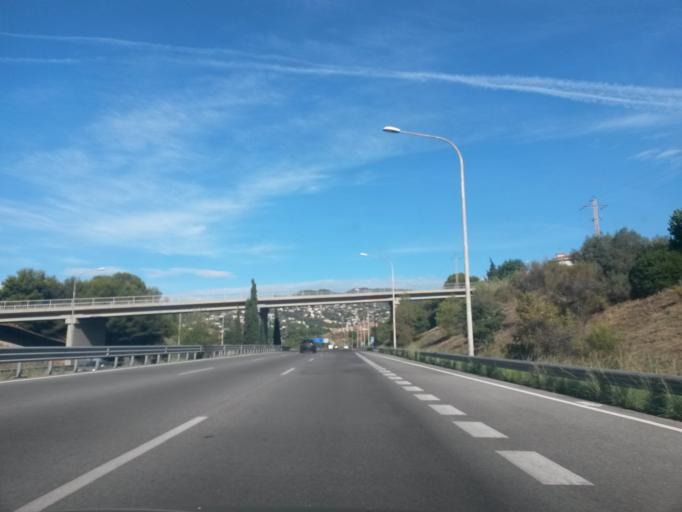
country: ES
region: Catalonia
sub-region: Provincia de Barcelona
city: El Masnou
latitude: 41.4878
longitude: 2.3109
